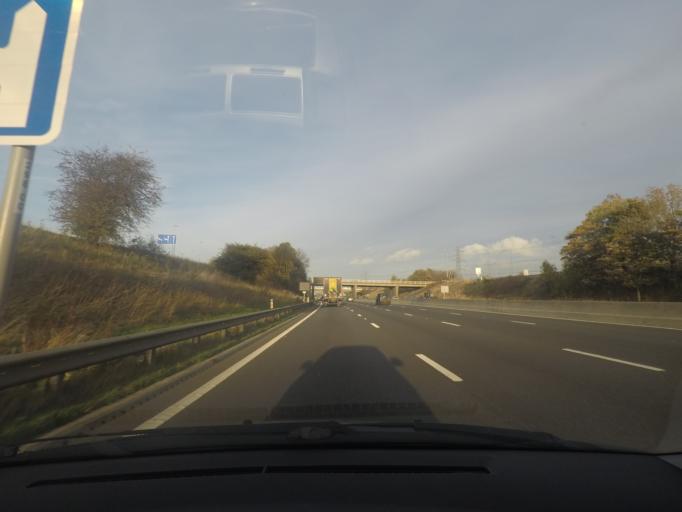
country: GB
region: England
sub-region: City and Borough of Leeds
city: Lofthouse
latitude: 53.7145
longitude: -1.5382
